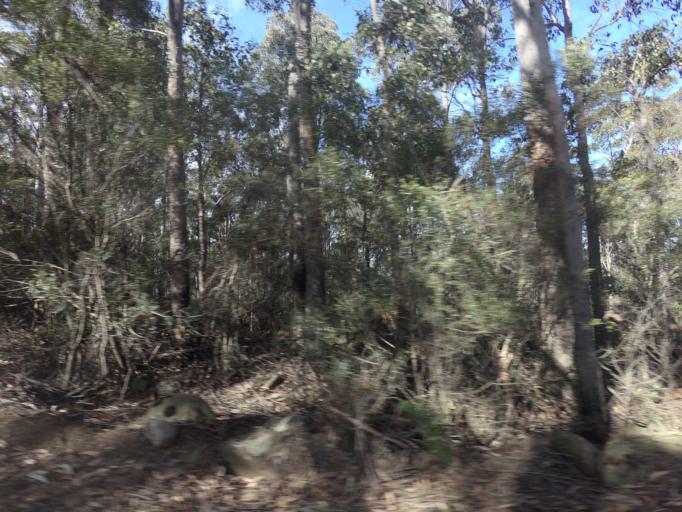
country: AU
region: Tasmania
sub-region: Sorell
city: Sorell
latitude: -42.4905
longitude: 147.4816
